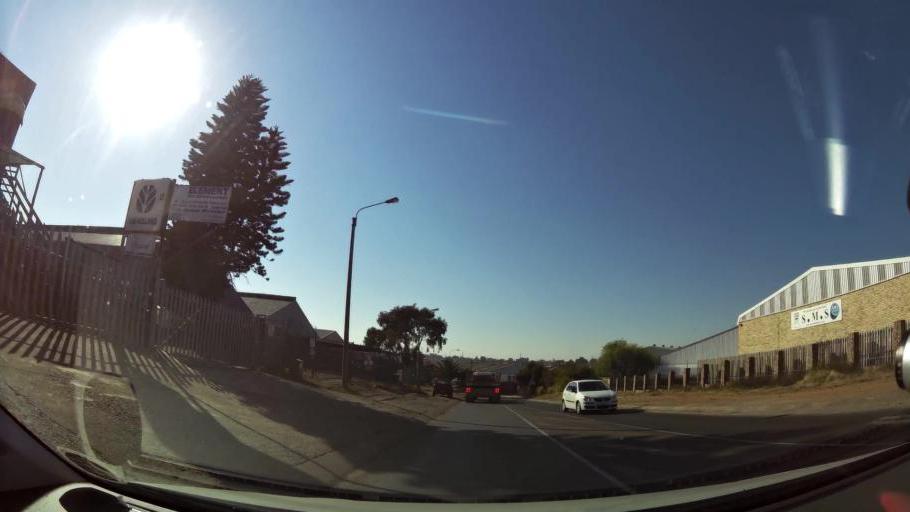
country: ZA
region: Gauteng
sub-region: City of Johannesburg Metropolitan Municipality
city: Modderfontein
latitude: -26.0690
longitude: 28.1911
